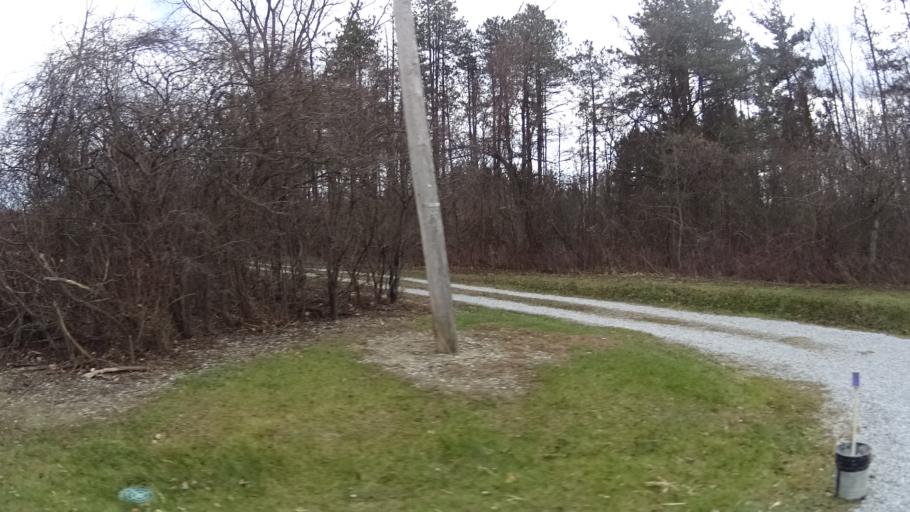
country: US
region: Ohio
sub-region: Lorain County
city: Oberlin
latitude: 41.2605
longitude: -82.2072
